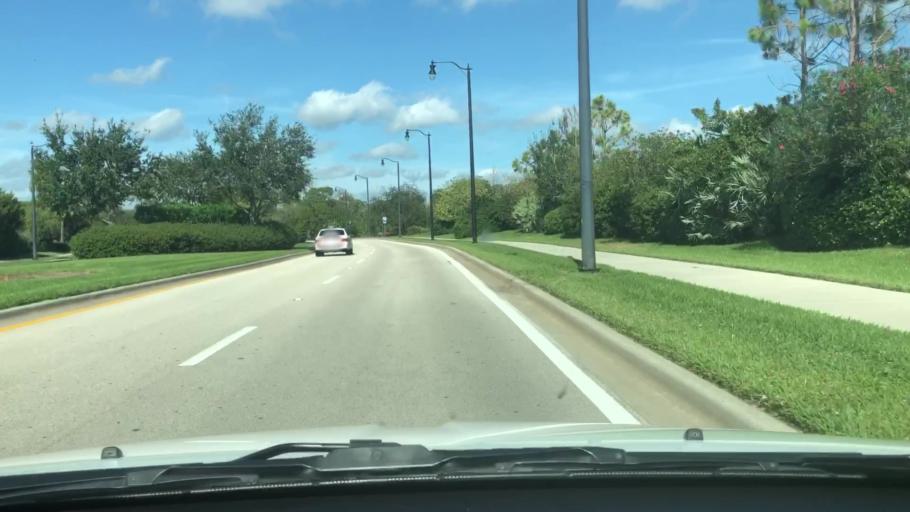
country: US
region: Florida
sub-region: Saint Lucie County
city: Port Saint Lucie
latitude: 27.2903
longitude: -80.4382
